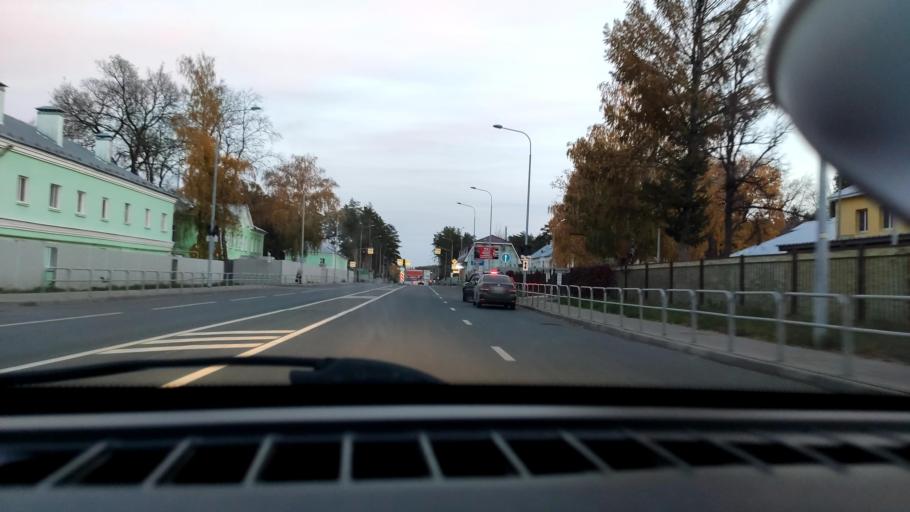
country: RU
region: Samara
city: Samara
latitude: 53.2674
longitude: 50.2394
